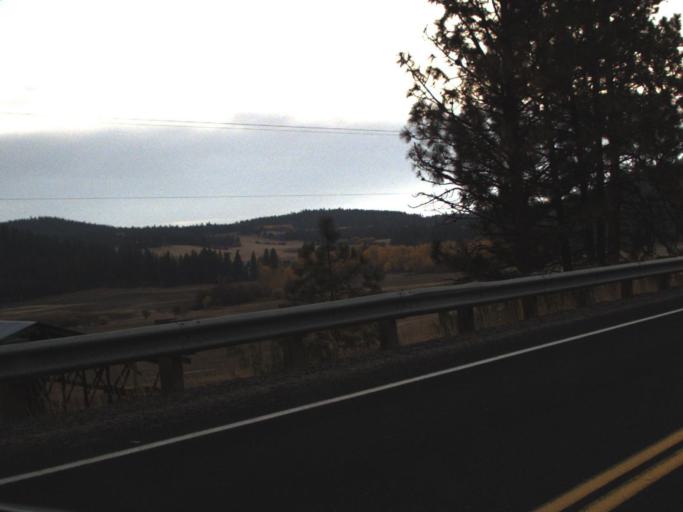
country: US
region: Washington
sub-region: Lincoln County
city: Davenport
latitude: 48.0073
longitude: -118.2629
